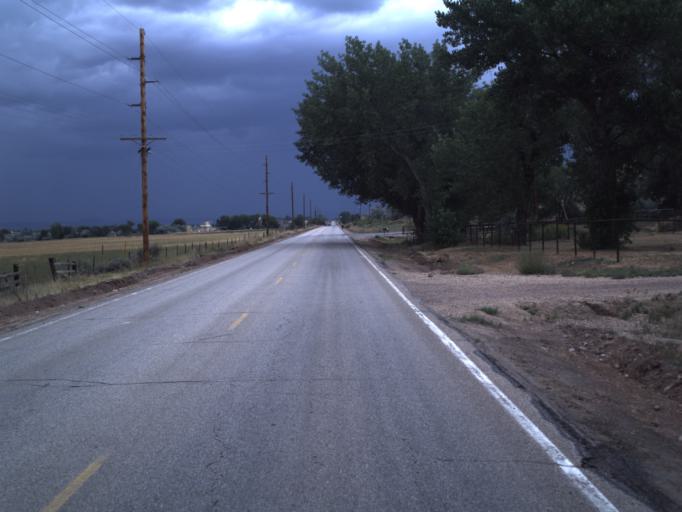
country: US
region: Utah
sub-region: Duchesne County
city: Roosevelt
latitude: 40.3200
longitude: -110.0150
